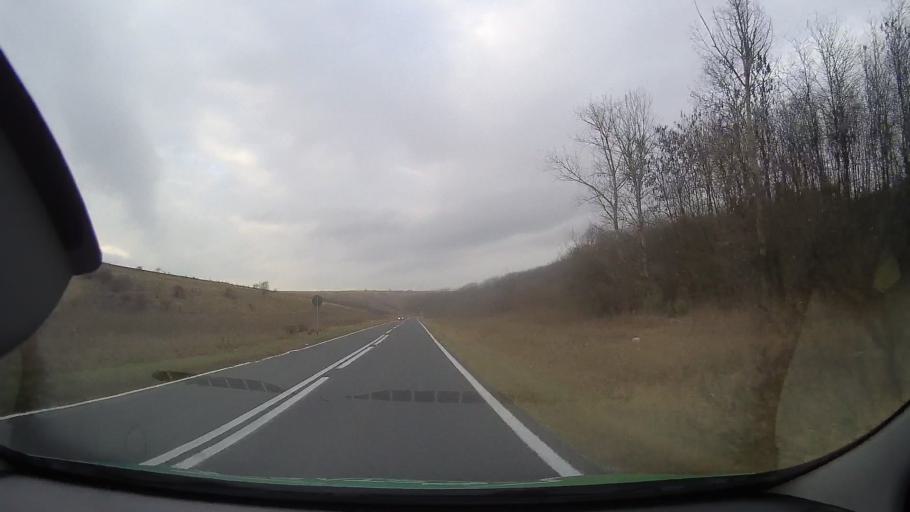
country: RO
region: Constanta
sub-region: Comuna Deleni
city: Deleni
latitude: 44.1007
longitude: 28.0288
